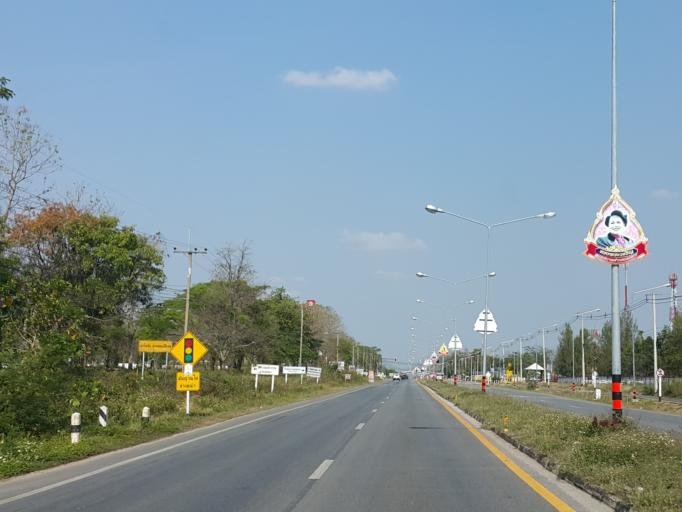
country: TH
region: Lampang
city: Mae Mo
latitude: 18.2722
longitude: 99.6478
